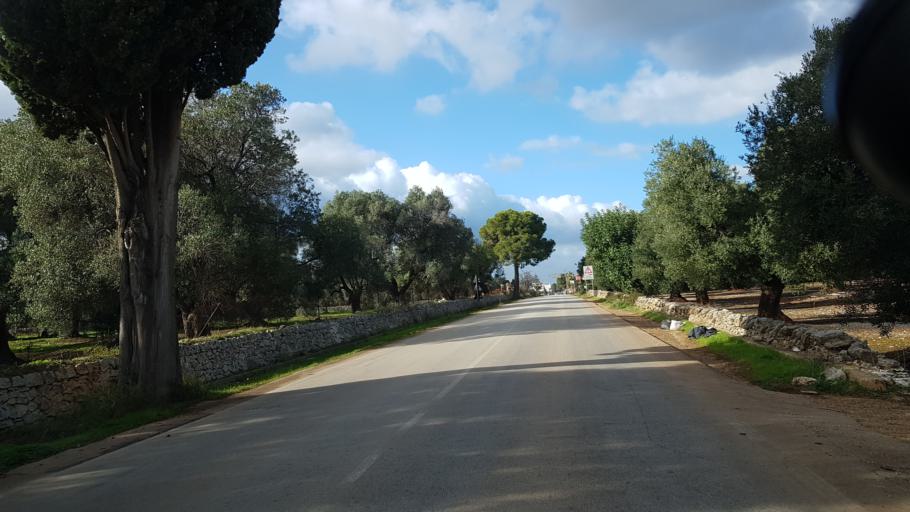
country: IT
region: Apulia
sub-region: Provincia di Brindisi
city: Montalbano
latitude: 40.7792
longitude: 17.4874
